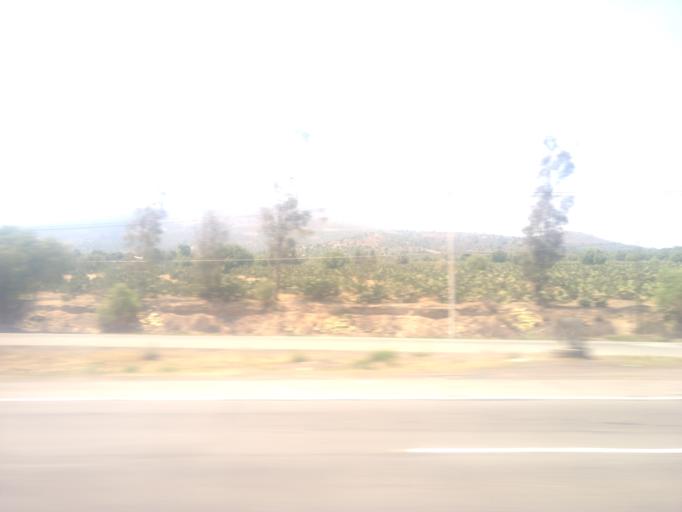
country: MX
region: Mexico
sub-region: Axapusco
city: Colonia los Remedios
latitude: 19.7274
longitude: -98.7801
